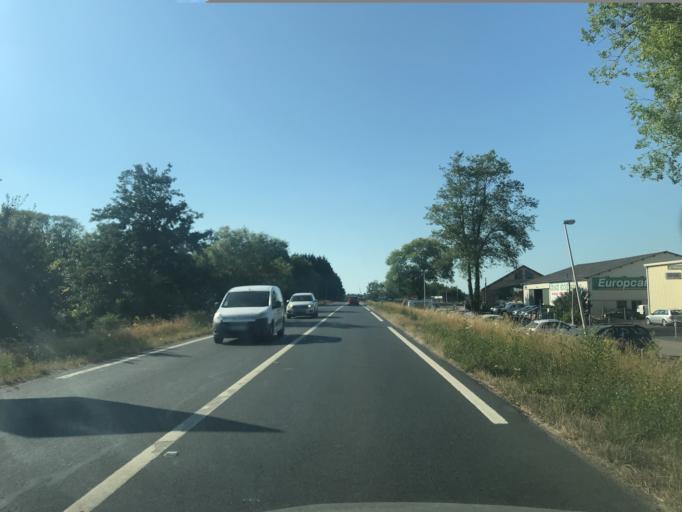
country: FR
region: Lower Normandy
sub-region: Departement du Calvados
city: Touques
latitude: 49.3405
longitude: 0.0976
